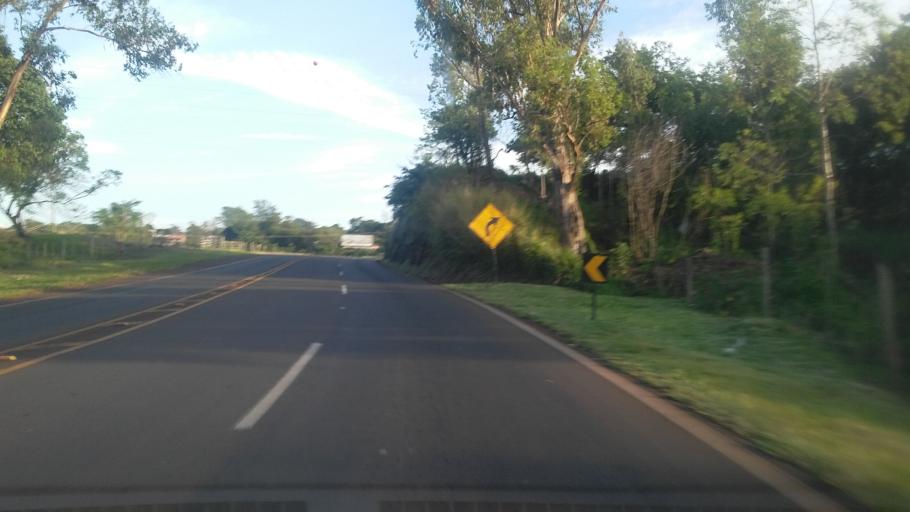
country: BR
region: Parana
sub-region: Assai
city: Assai
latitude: -23.2053
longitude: -50.6548
